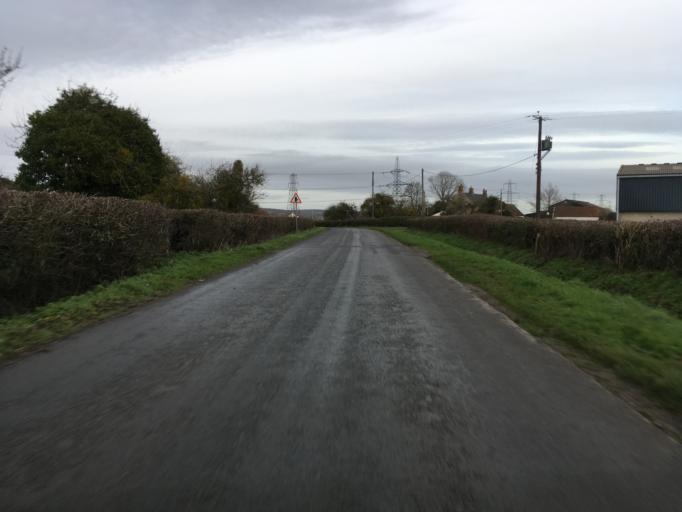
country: GB
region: Wales
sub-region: Monmouthshire
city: Magor
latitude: 51.5658
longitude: -2.8211
